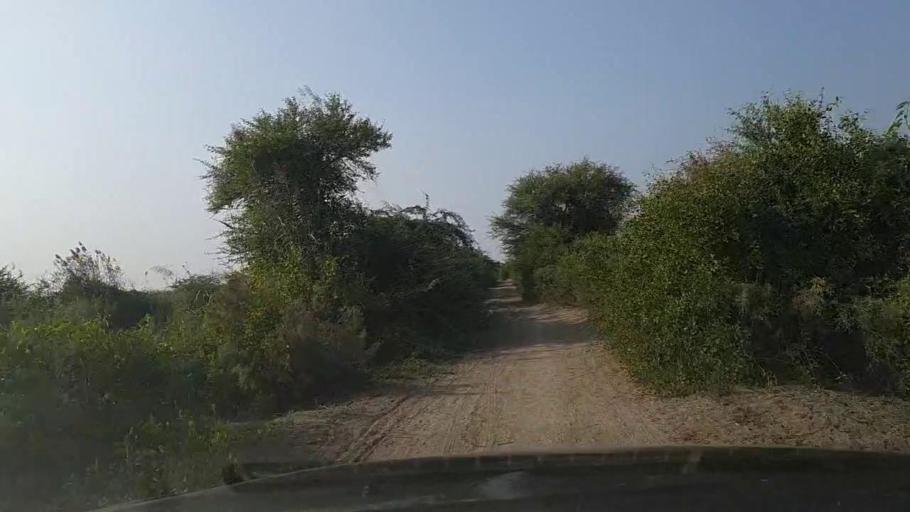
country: PK
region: Sindh
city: Mirpur Batoro
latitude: 24.6473
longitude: 68.2790
